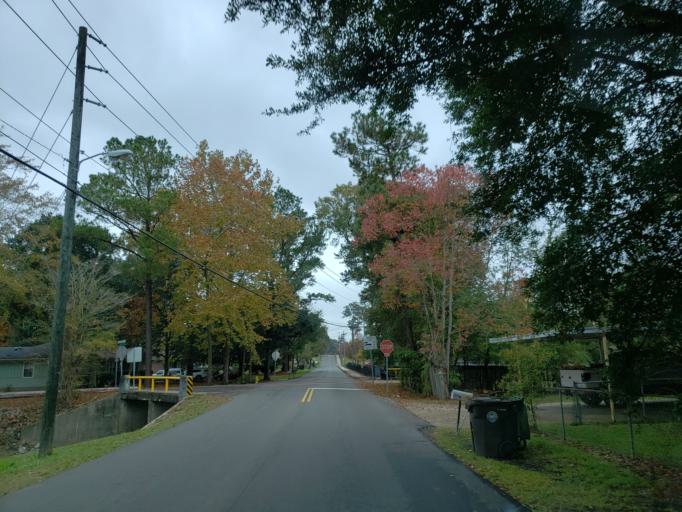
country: US
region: Mississippi
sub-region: Forrest County
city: Hattiesburg
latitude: 31.3207
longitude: -89.3185
